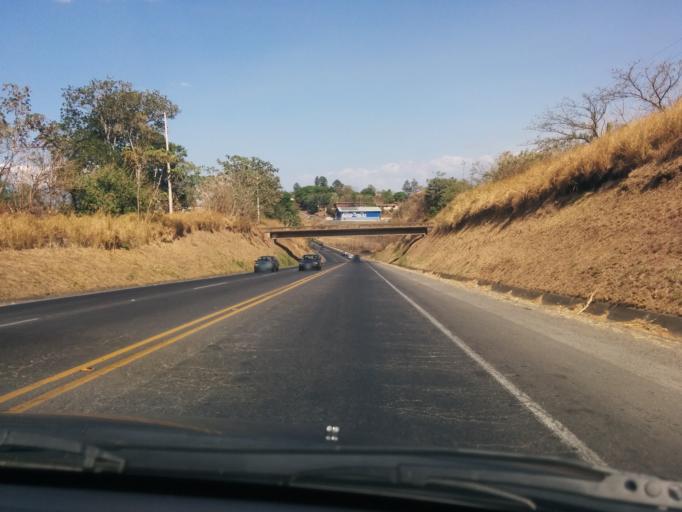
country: CR
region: Alajuela
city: Atenas
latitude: 10.0161
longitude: -84.3529
